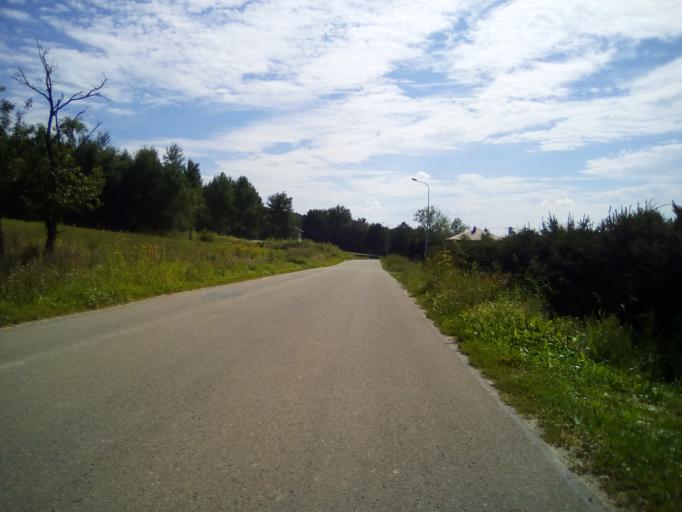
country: PL
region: Subcarpathian Voivodeship
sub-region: Powiat strzyzowski
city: Konieczkowa
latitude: 49.8221
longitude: 21.9267
